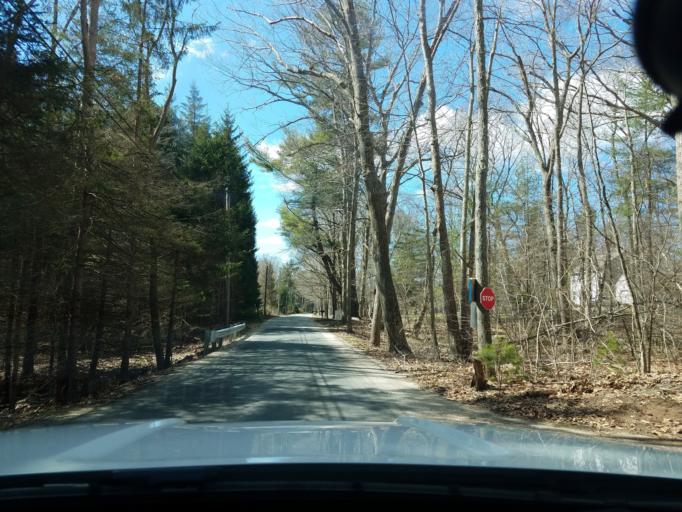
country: US
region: Connecticut
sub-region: Tolland County
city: Coventry Lake
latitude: 41.7651
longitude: -72.3936
